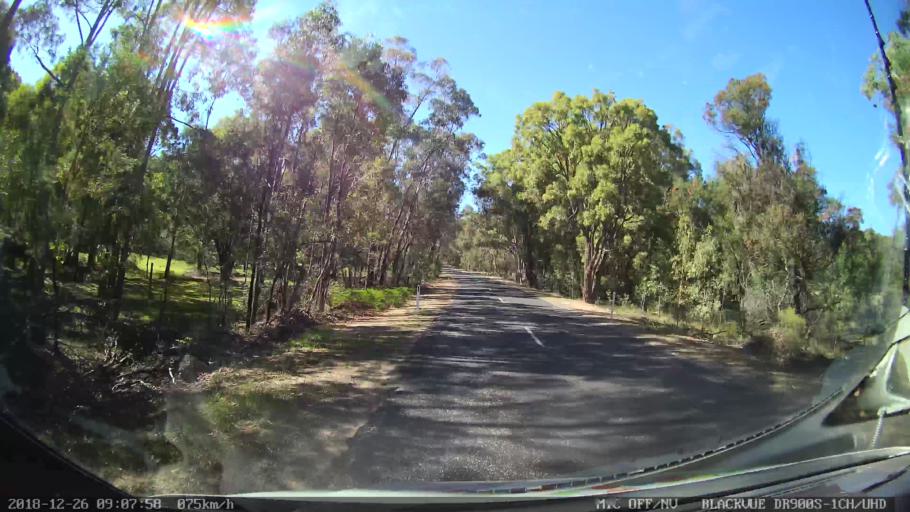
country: AU
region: New South Wales
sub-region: Mid-Western Regional
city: Kandos
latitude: -32.7115
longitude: 150.0030
